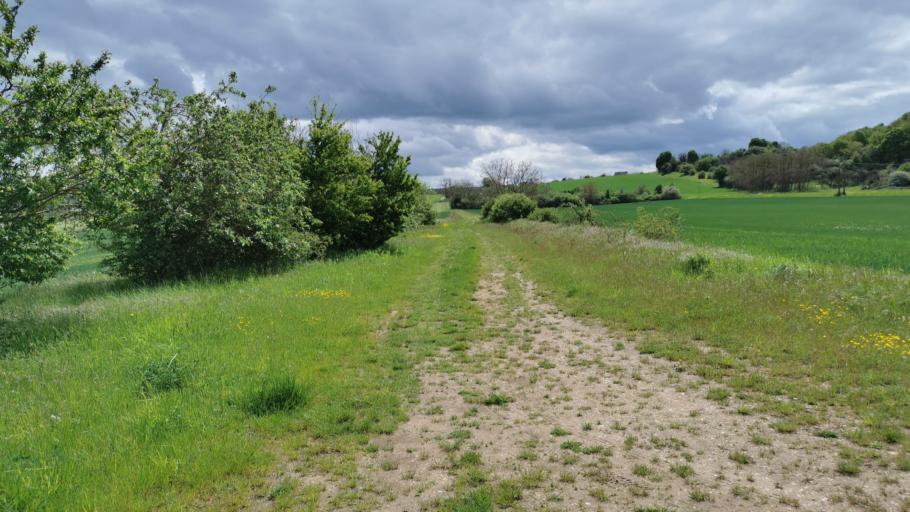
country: FR
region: Bourgogne
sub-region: Departement de l'Yonne
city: Saint-Julien-du-Sault
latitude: 48.0452
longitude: 3.3025
